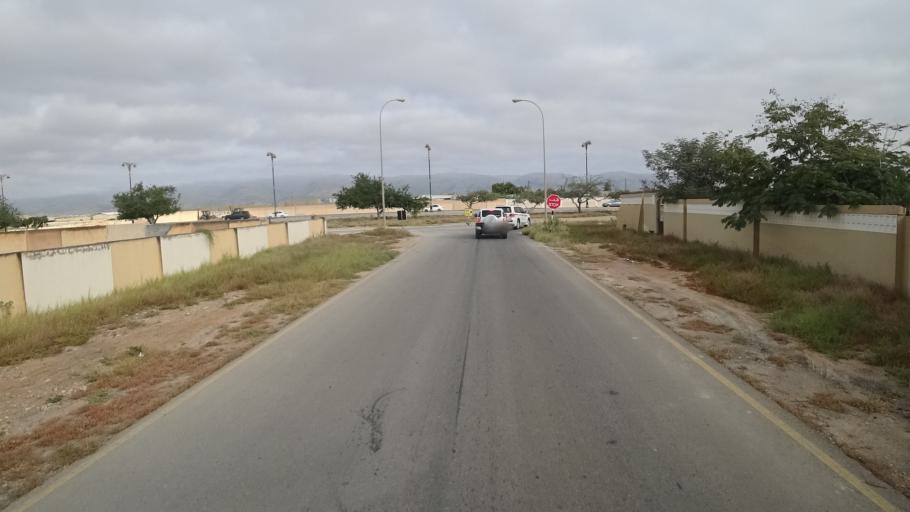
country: OM
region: Zufar
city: Salalah
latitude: 17.0098
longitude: 54.0460
